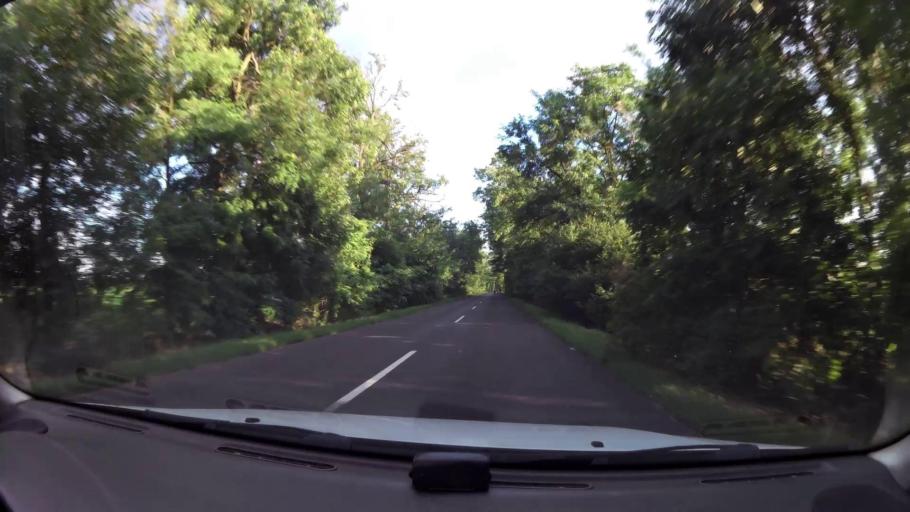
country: HU
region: Pest
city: Tapiosag
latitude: 47.4203
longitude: 19.6094
